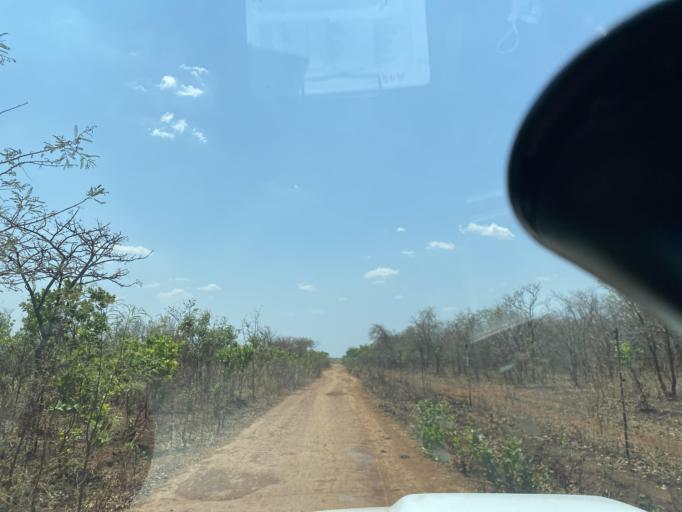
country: ZM
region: Lusaka
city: Lusaka
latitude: -15.5027
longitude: 27.9699
